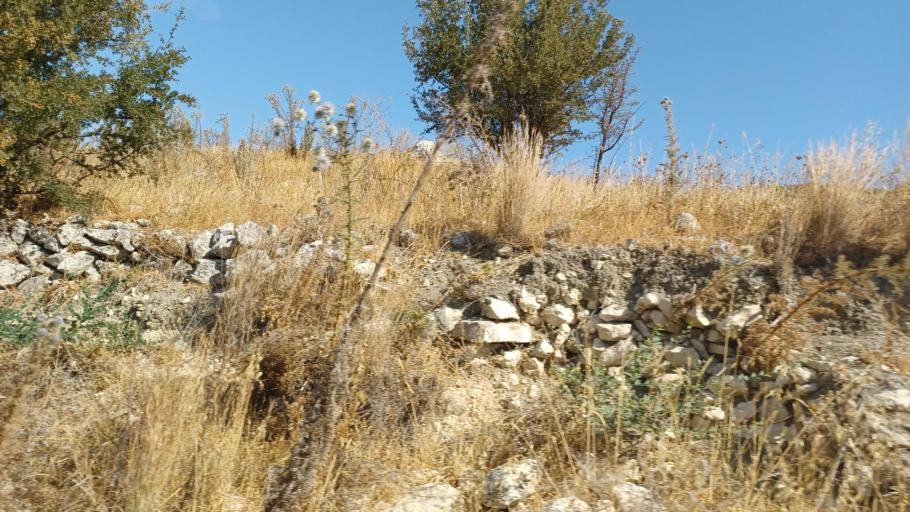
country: CY
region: Pafos
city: Polis
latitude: 34.9710
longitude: 32.4965
